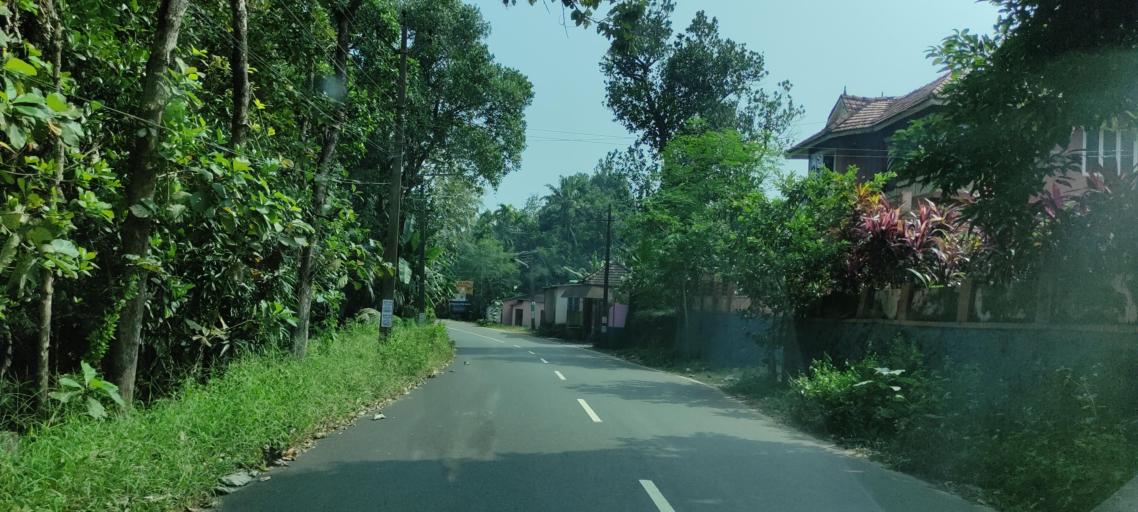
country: IN
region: Kerala
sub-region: Pattanamtitta
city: Adur
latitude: 9.2379
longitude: 76.6946
